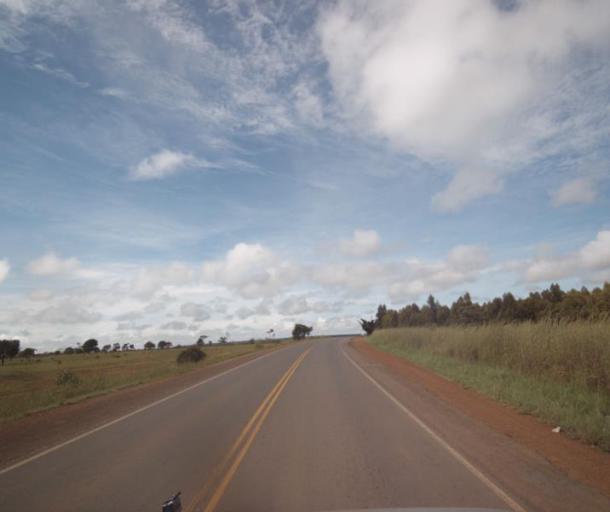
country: BR
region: Goias
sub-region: Pirenopolis
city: Pirenopolis
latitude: -16.0163
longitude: -48.8375
